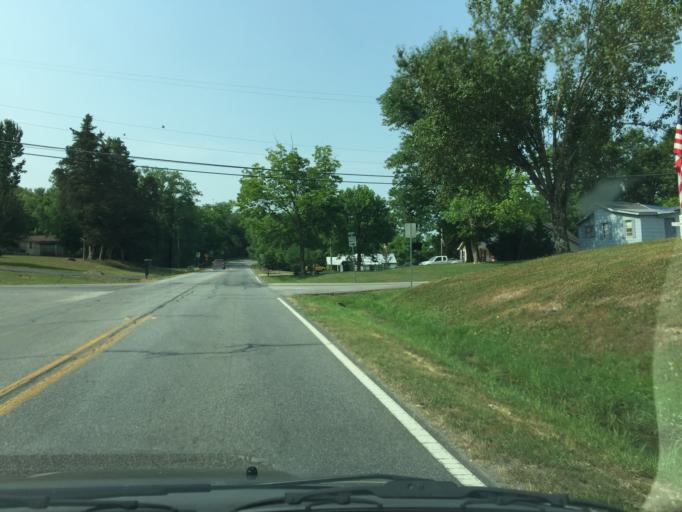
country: US
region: Georgia
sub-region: Catoosa County
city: Ringgold
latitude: 34.9210
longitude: -85.1043
